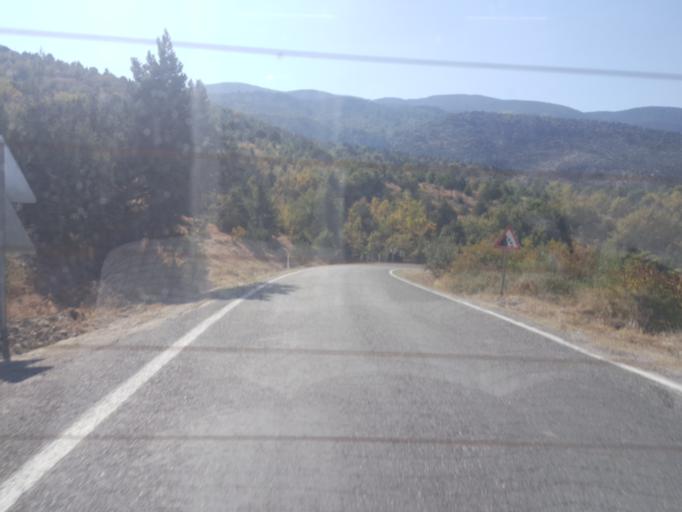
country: TR
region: Kastamonu
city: Tosya
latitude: 40.9953
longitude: 34.1682
